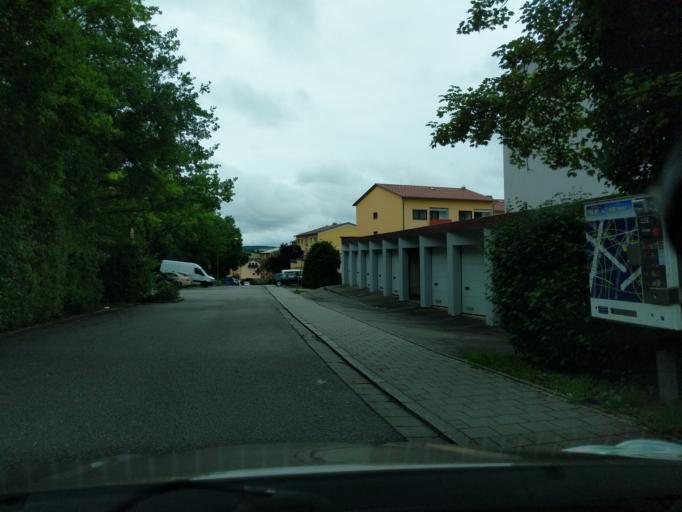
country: DE
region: Bavaria
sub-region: Upper Palatinate
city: Lappersdorf
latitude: 49.0613
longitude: 12.0834
